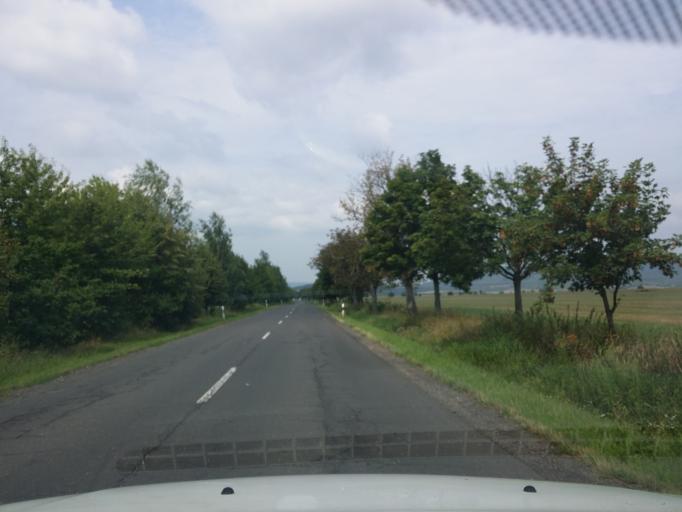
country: HU
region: Borsod-Abauj-Zemplen
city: Satoraljaujhely
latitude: 48.4677
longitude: 21.5832
